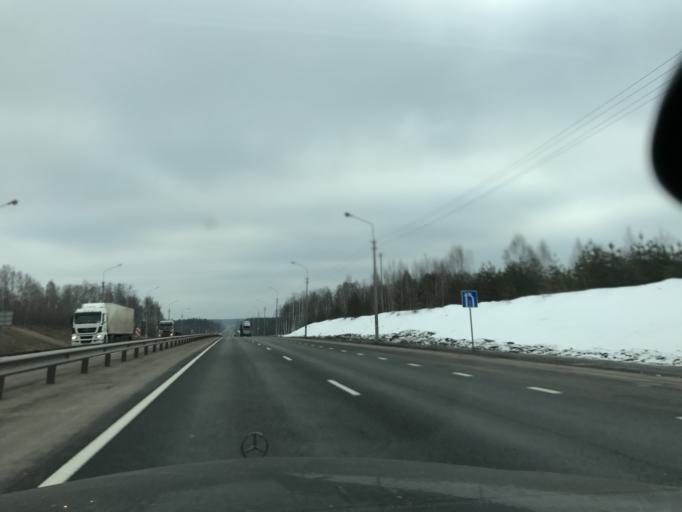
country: RU
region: Vladimir
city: Sudogda
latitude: 56.1039
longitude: 40.7800
